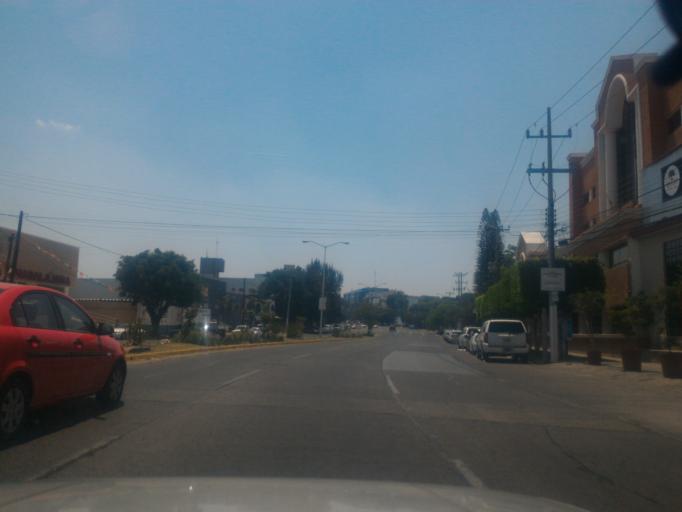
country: MX
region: Jalisco
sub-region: Zapopan
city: Zapopan
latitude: 20.7134
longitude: -103.3837
